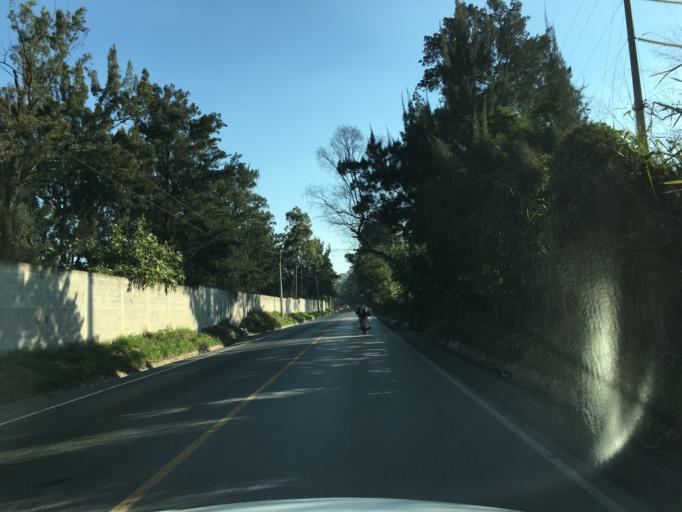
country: GT
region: Guatemala
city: Villa Nueva
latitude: 14.5259
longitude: -90.6168
